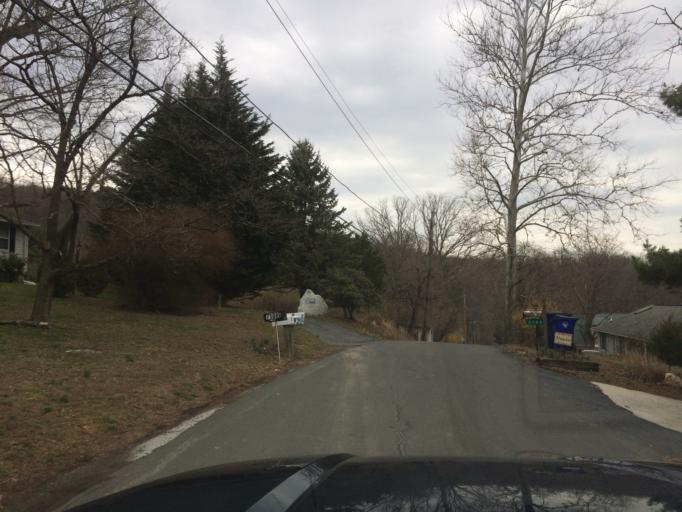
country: US
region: Maryland
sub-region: Frederick County
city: Braddock Heights
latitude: 39.4281
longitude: -77.4926
